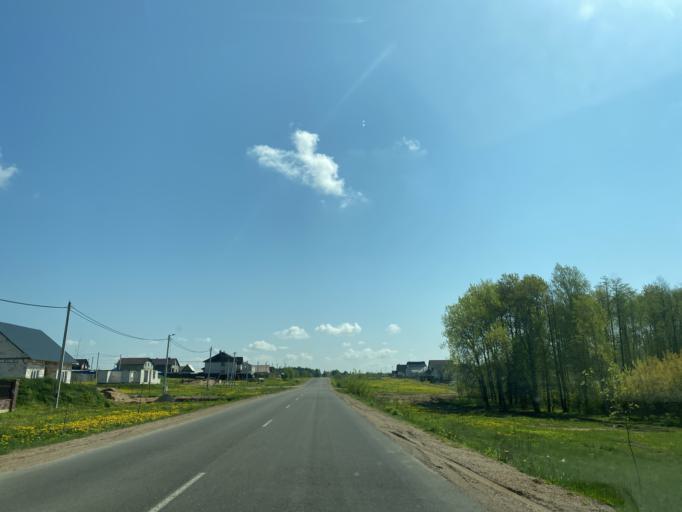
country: BY
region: Minsk
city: Horad Barysaw
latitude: 54.1789
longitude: 28.5586
